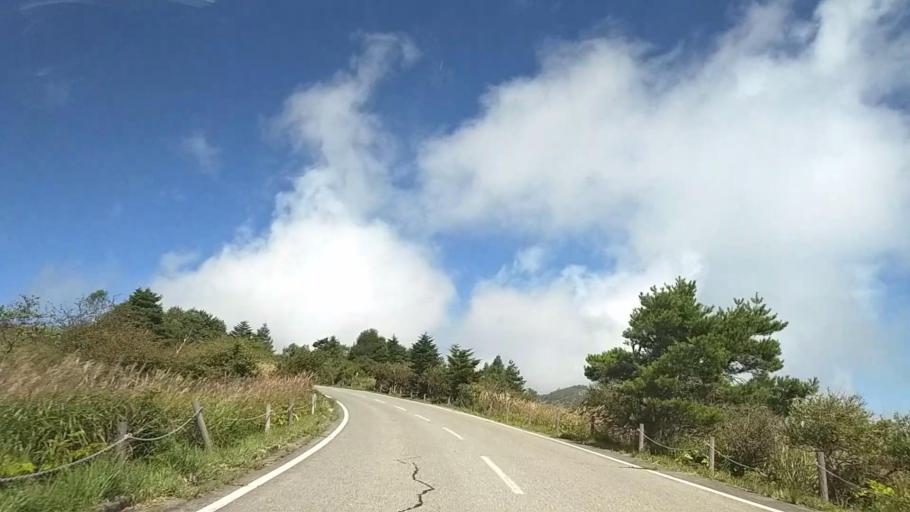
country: JP
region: Nagano
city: Suwa
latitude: 36.1154
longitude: 138.1633
